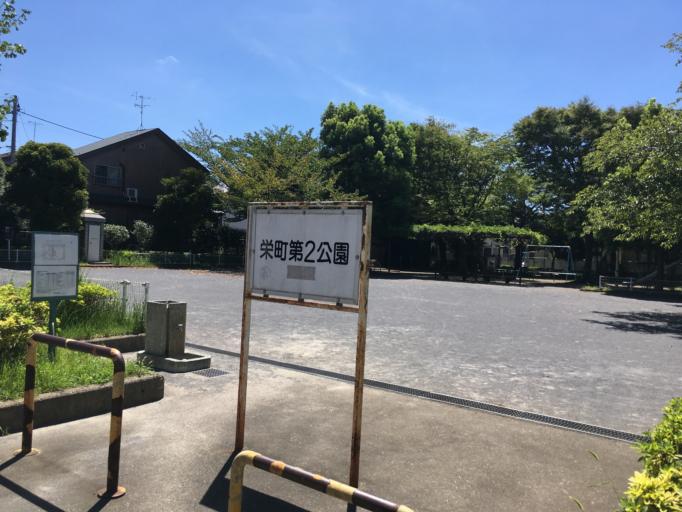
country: JP
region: Chiba
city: Matsudo
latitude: 35.8046
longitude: 139.9030
